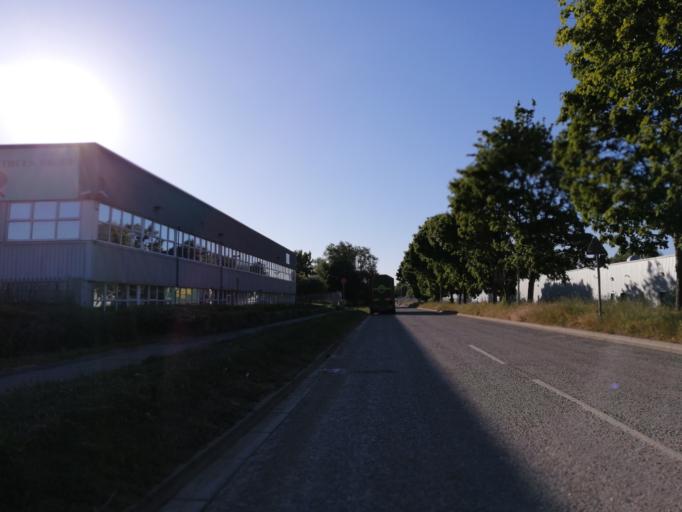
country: GB
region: England
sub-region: Peterborough
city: Marholm
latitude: 52.6067
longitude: -0.2836
